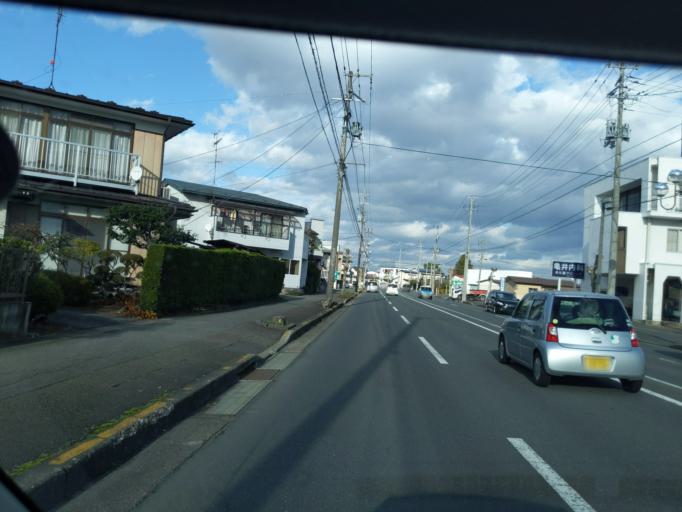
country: JP
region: Iwate
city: Mizusawa
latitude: 39.1329
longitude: 141.1540
